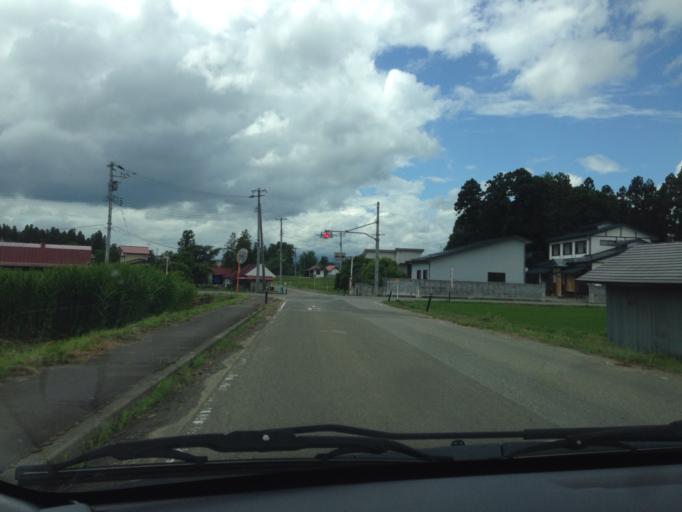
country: JP
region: Fukushima
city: Kitakata
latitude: 37.6130
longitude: 139.8986
